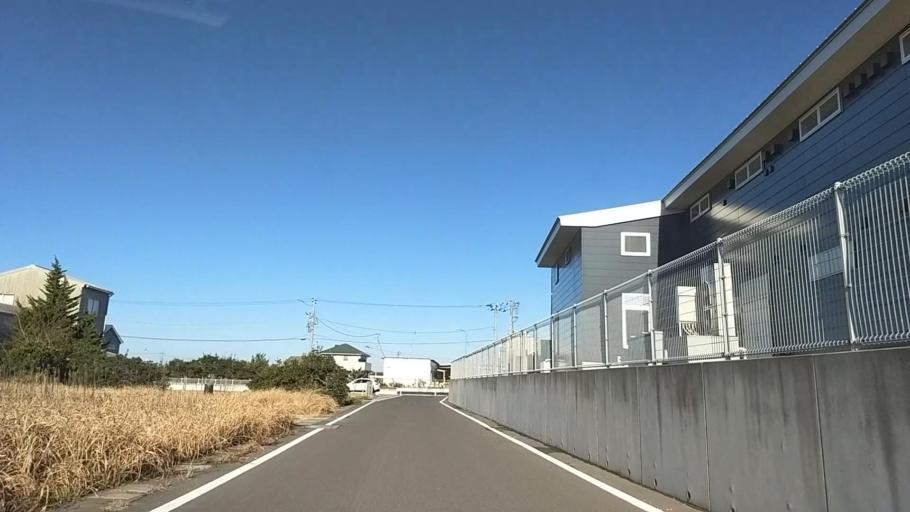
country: JP
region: Chiba
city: Naruto
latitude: 35.5383
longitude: 140.4570
